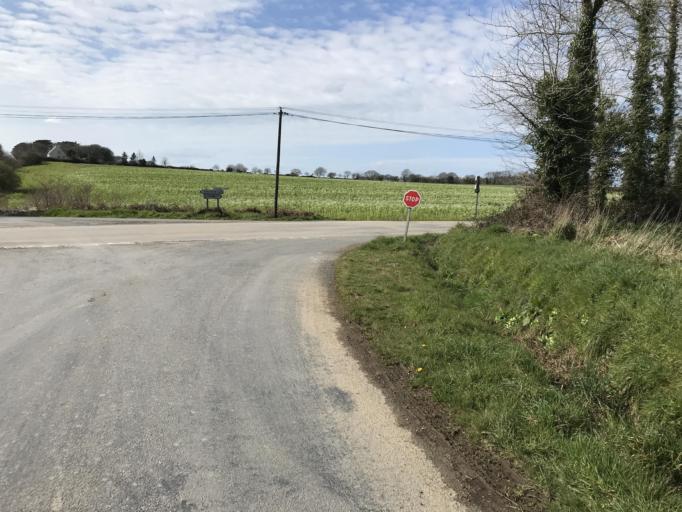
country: FR
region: Brittany
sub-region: Departement du Finistere
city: Loperhet
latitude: 48.3722
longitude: -4.2838
